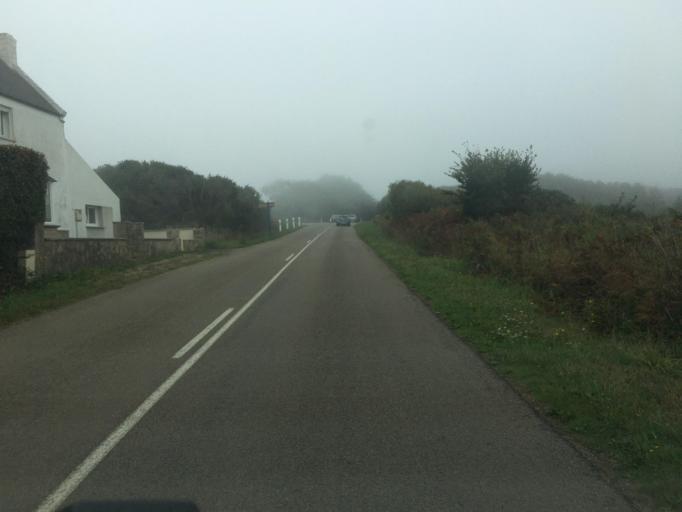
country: FR
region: Brittany
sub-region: Departement du Finistere
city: Plogoff
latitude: 48.0570
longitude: -4.6697
